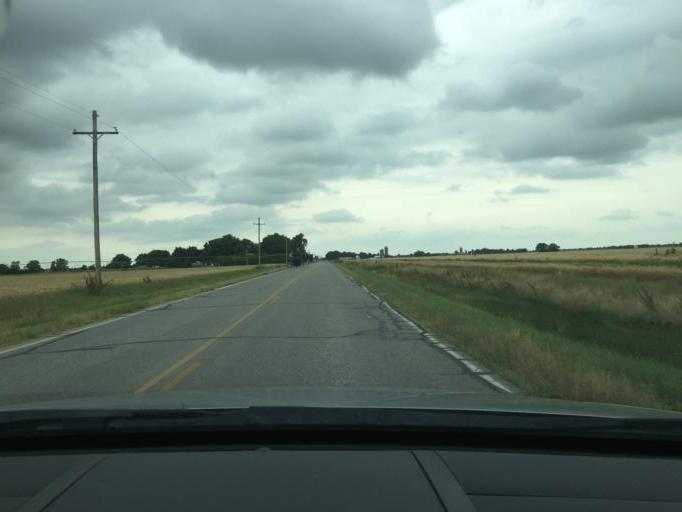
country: US
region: Kansas
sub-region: Reno County
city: South Hutchinson
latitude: 37.9710
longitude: -98.0138
